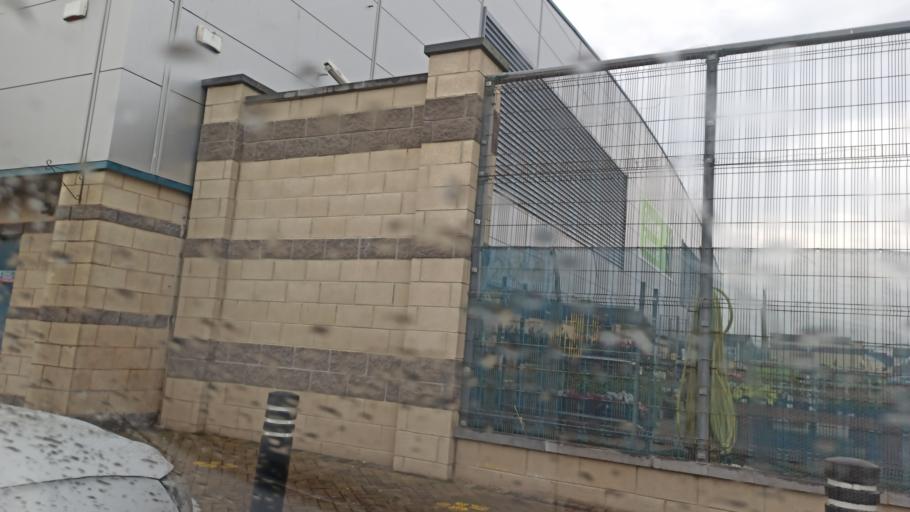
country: IE
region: Munster
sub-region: South Tipperary
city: Cluain Meala
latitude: 52.3568
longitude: -7.7350
